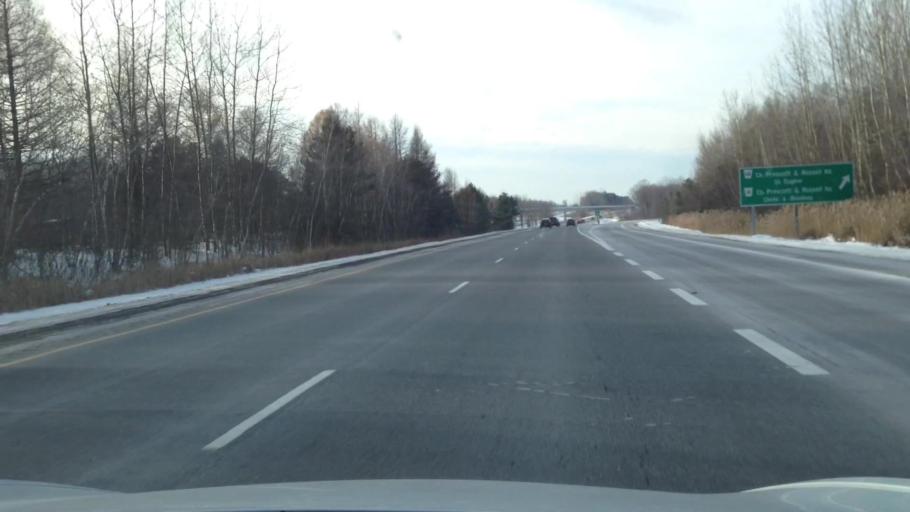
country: CA
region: Quebec
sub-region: Laurentides
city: Brownsburg-Chatham
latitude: 45.5520
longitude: -74.4431
